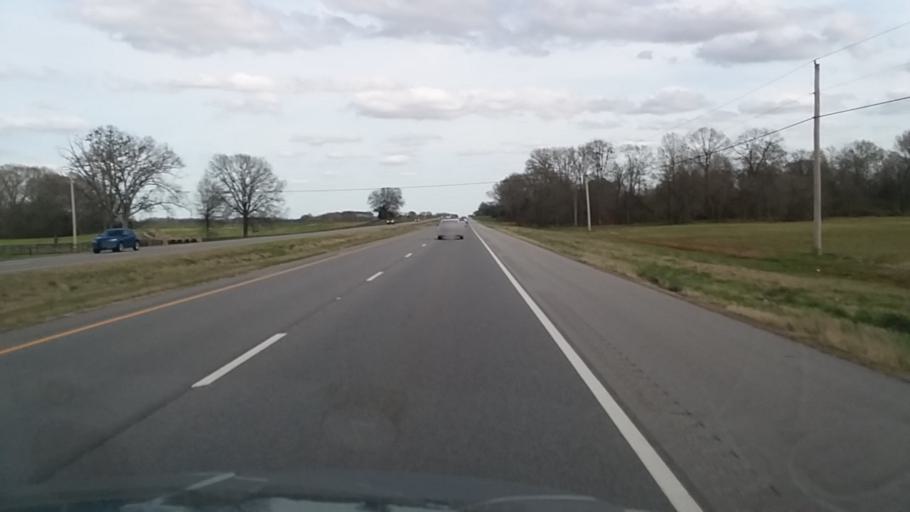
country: US
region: Alabama
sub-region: Colbert County
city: Muscle Shoals
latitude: 34.6841
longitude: -87.5442
